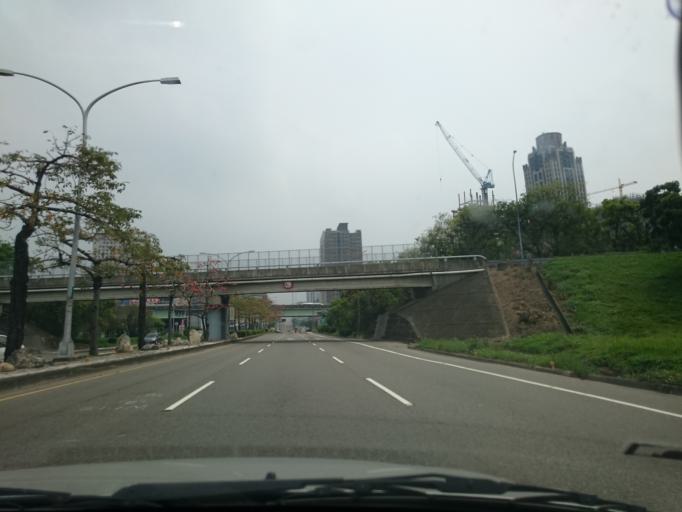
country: TW
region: Taiwan
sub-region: Taichung City
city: Taichung
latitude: 24.1744
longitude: 120.6320
